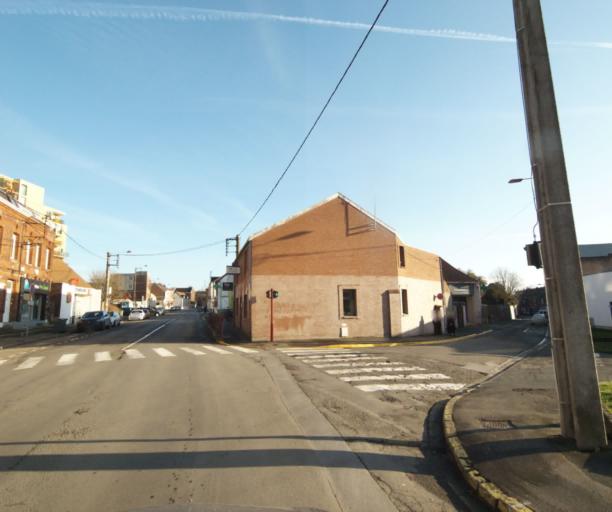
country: FR
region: Nord-Pas-de-Calais
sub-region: Departement du Nord
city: Valenciennes
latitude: 50.3511
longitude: 3.5406
